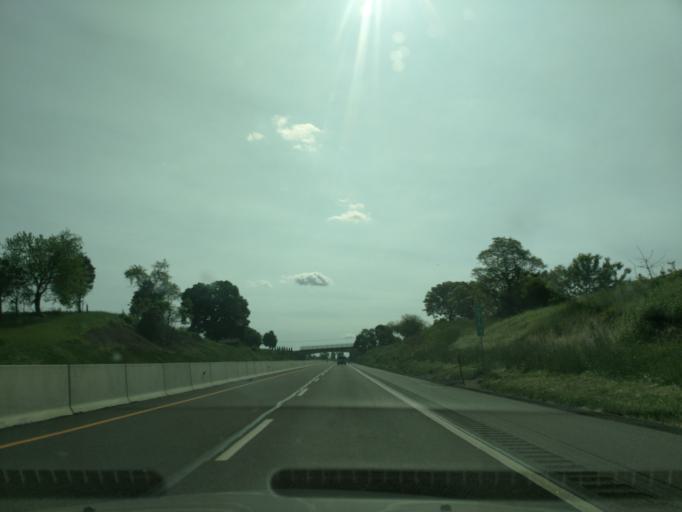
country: US
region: Pennsylvania
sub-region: Lancaster County
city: Clay
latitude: 40.2408
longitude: -76.2518
